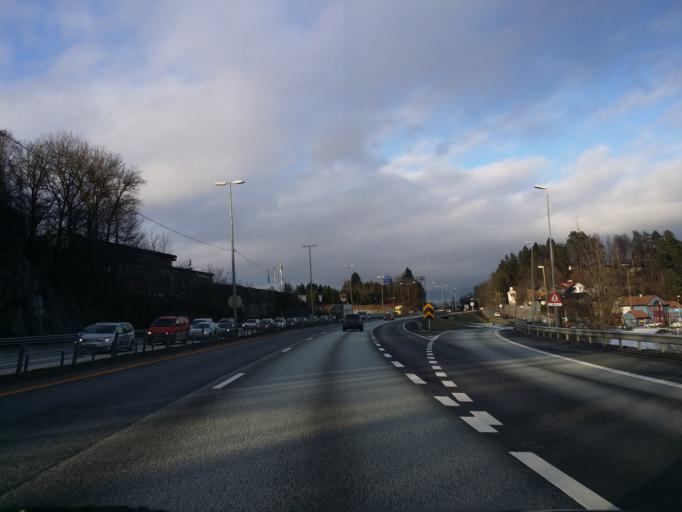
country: NO
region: Akershus
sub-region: Asker
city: Billingstad
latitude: 59.8543
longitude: 10.4794
